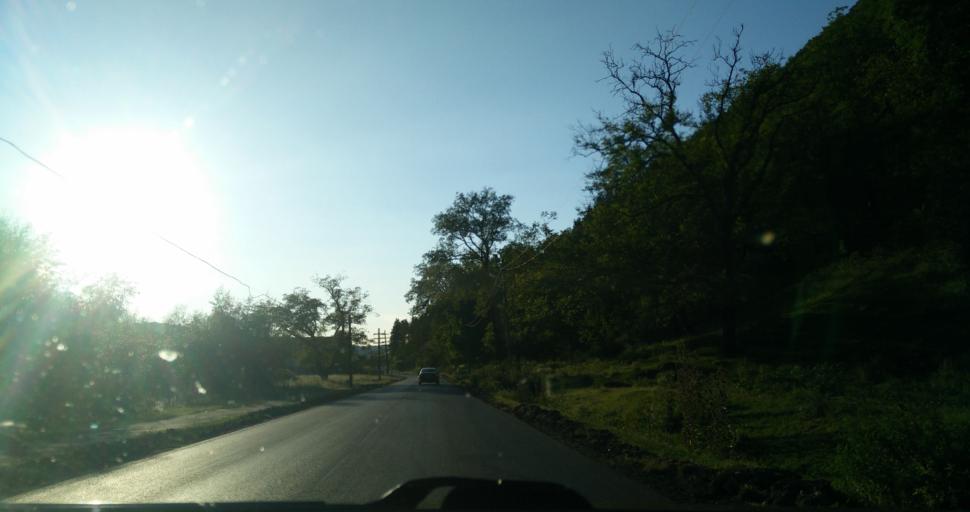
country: RO
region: Bihor
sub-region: Oras Nucet
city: Nucet
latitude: 46.4836
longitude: 22.5705
